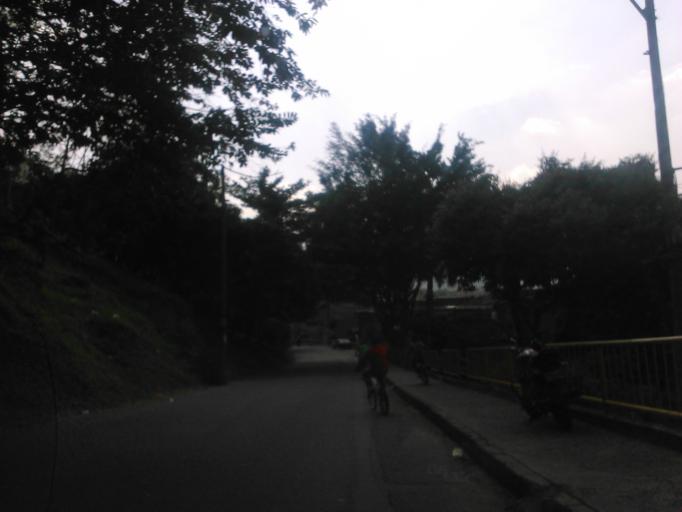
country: CO
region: Antioquia
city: Medellin
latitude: 6.2538
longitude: -75.6163
